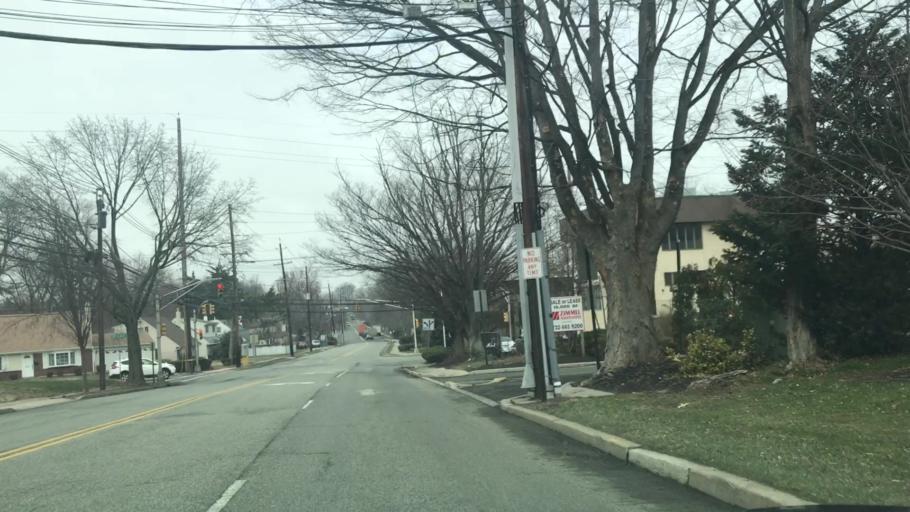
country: US
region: New Jersey
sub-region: Bergen County
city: Maywood
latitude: 40.9156
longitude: -74.0630
